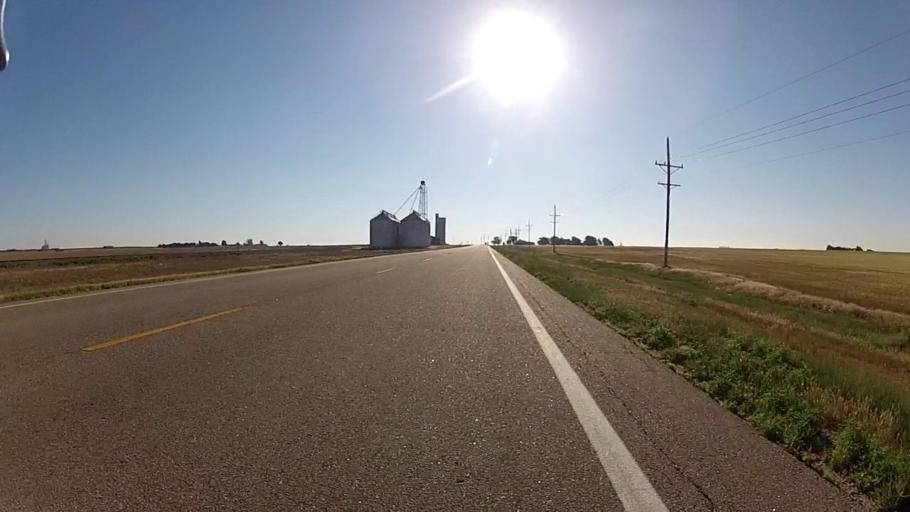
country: US
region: Kansas
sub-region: Haskell County
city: Sublette
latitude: 37.5144
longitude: -100.7319
